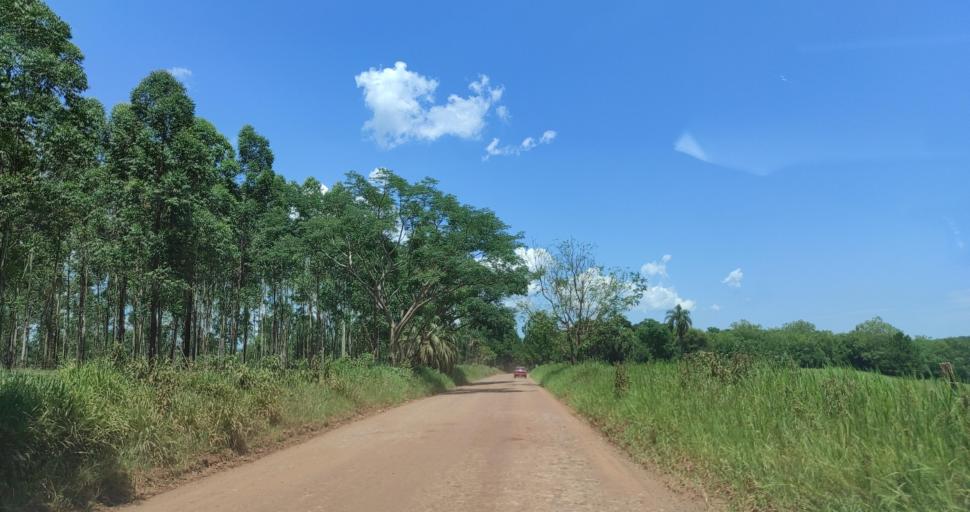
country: AR
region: Misiones
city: Ruiz de Montoya
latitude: -27.0421
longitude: -55.0260
